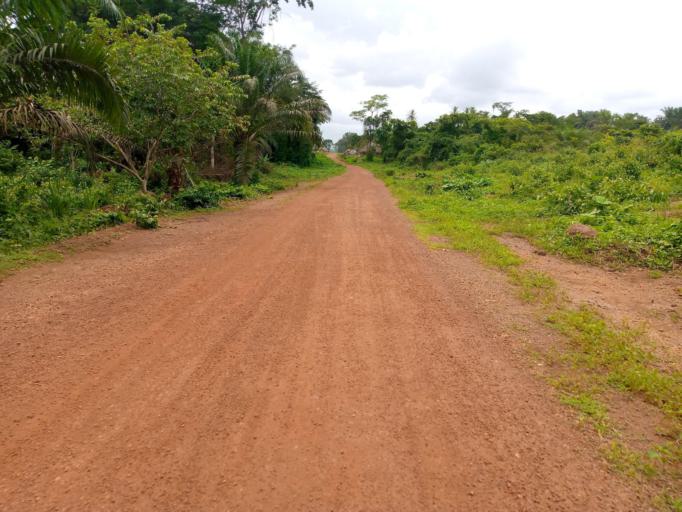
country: SL
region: Southern Province
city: Moyamba
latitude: 8.0868
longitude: -12.4491
